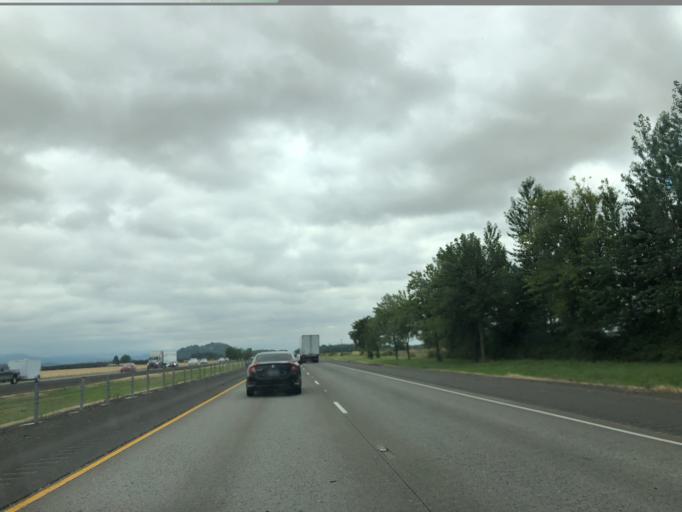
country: US
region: Oregon
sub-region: Linn County
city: Tangent
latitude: 44.4932
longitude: -123.0618
